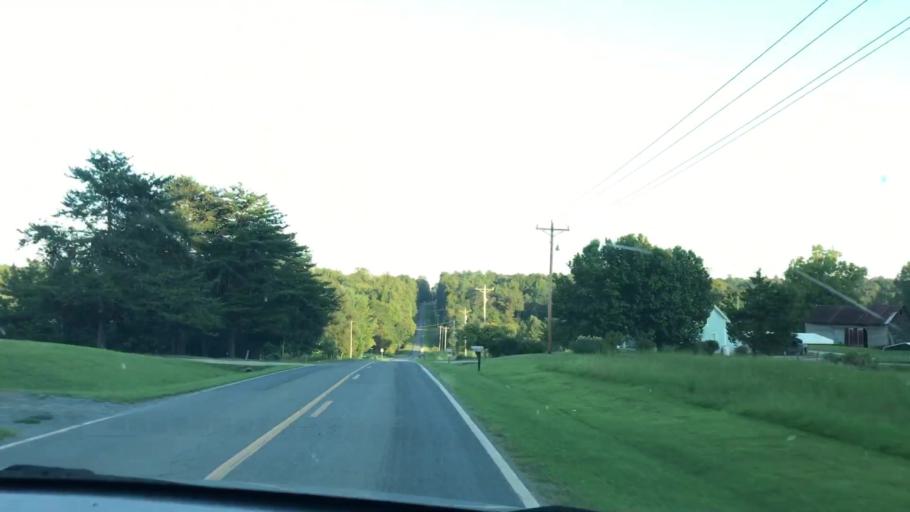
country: US
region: North Carolina
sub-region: Randolph County
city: Franklinville
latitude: 35.8105
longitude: -79.6901
